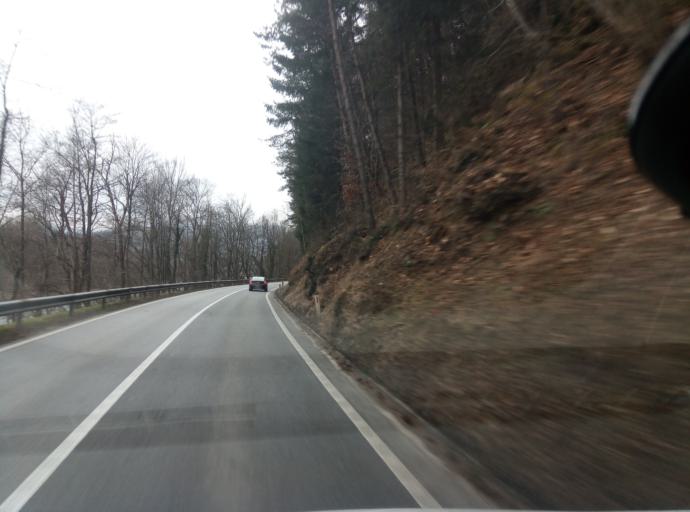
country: SI
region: Smartno pri Litiji
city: Smartno pri Litiji
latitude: 46.0694
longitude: 14.8626
